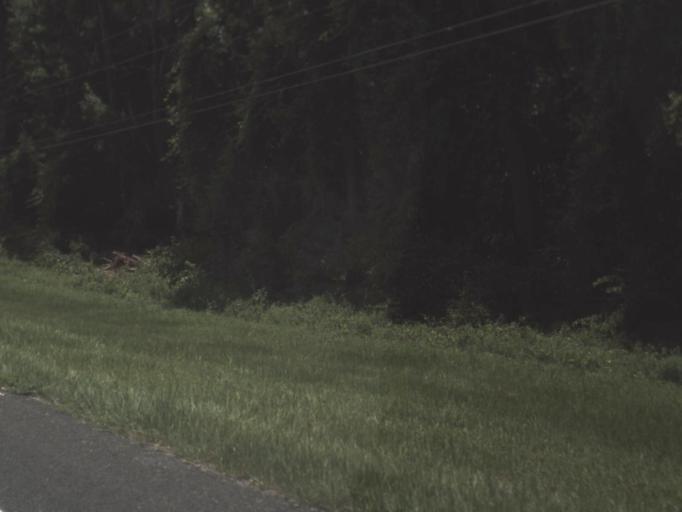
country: US
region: Florida
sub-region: Levy County
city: Manatee Road
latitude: 29.5767
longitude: -82.9164
